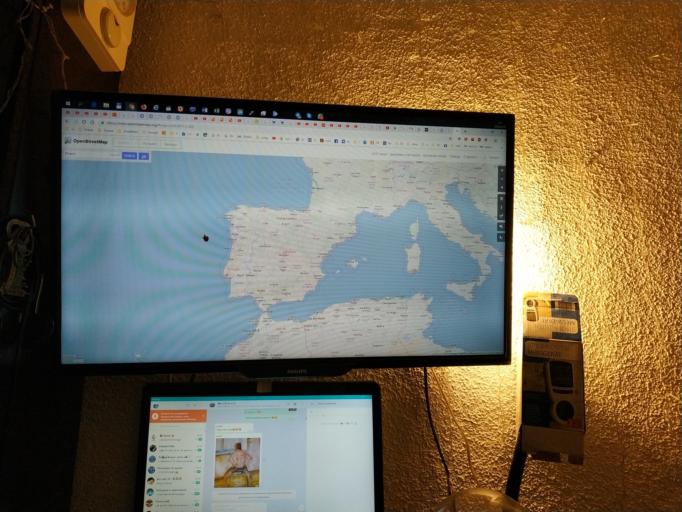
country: ES
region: Madrid
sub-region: Provincia de Madrid
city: Latina
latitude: 40.3968
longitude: -3.7701
